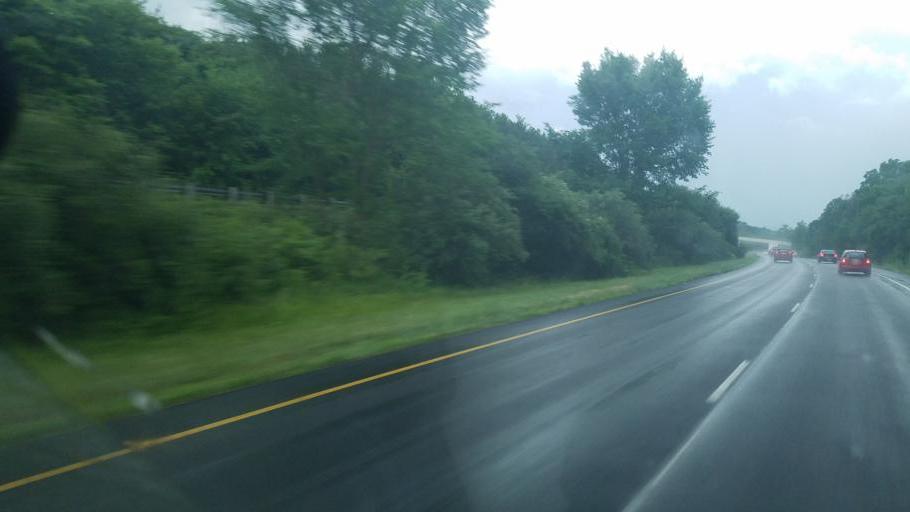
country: US
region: Ohio
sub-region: Summit County
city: Norton
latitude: 41.0735
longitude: -81.6659
